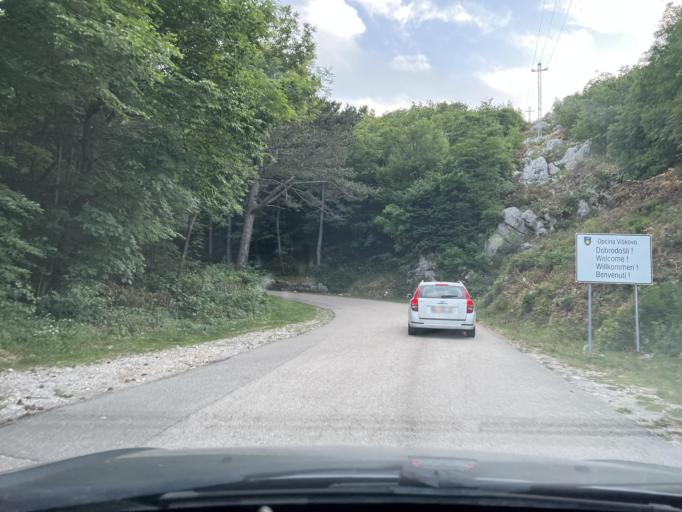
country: HR
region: Primorsko-Goranska
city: Marcelji
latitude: 45.3924
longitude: 14.4186
